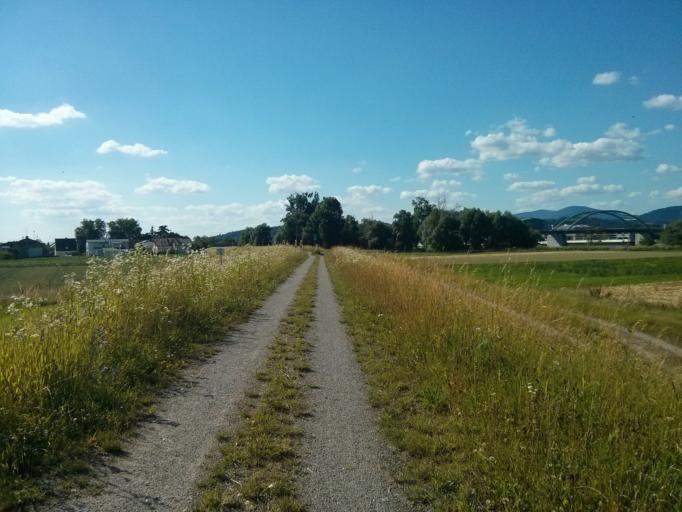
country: DE
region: Bavaria
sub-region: Lower Bavaria
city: Deggendorf
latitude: 48.8202
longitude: 12.9621
